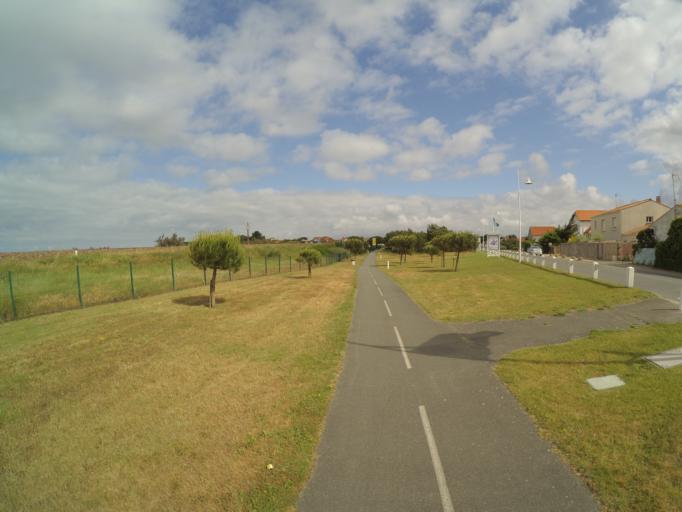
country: FR
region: Poitou-Charentes
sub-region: Departement de la Charente-Maritime
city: Angoulins
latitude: 46.0934
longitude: -1.0997
